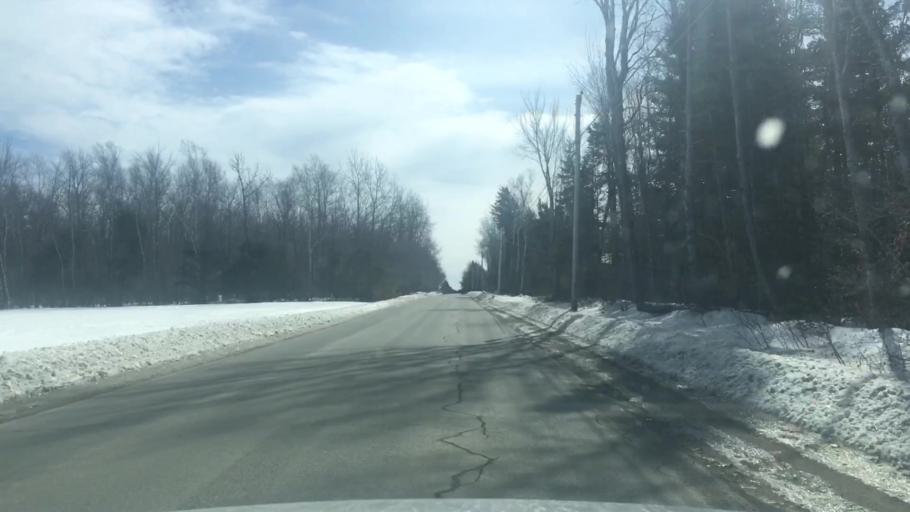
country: US
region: Maine
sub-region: Penobscot County
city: Holden
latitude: 44.7731
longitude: -68.6498
